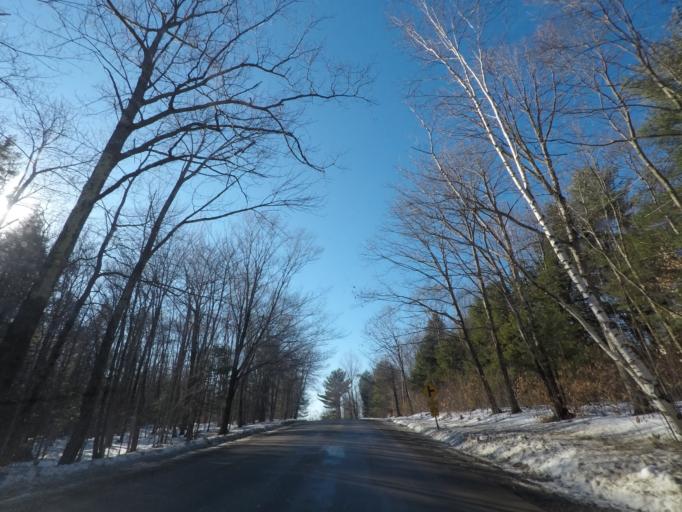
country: US
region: New York
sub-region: Rensselaer County
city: Averill Park
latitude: 42.6266
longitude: -73.5027
